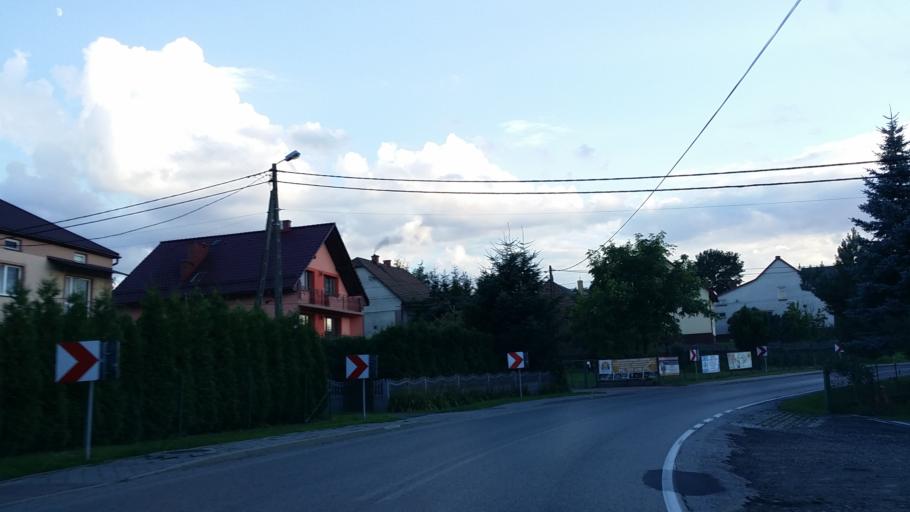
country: PL
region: Lesser Poland Voivodeship
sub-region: Powiat oswiecimski
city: Przeciszow
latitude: 50.0002
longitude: 19.3723
